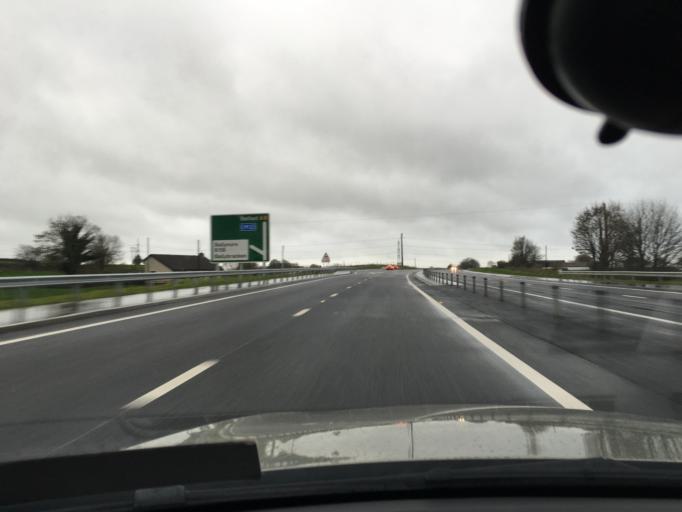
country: GB
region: Northern Ireland
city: Ballyclare
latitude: 54.7899
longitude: -5.9378
